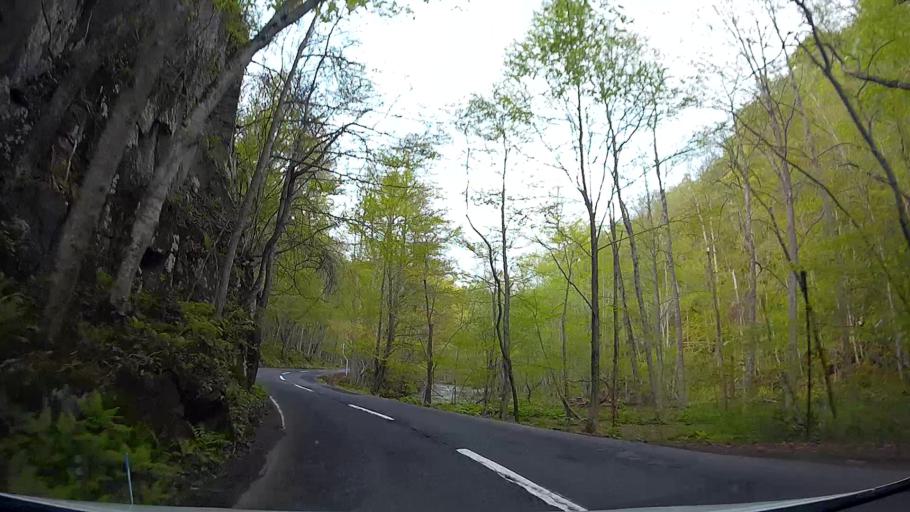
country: JP
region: Aomori
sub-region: Aomori Shi
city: Furudate
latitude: 40.5262
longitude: 140.9743
